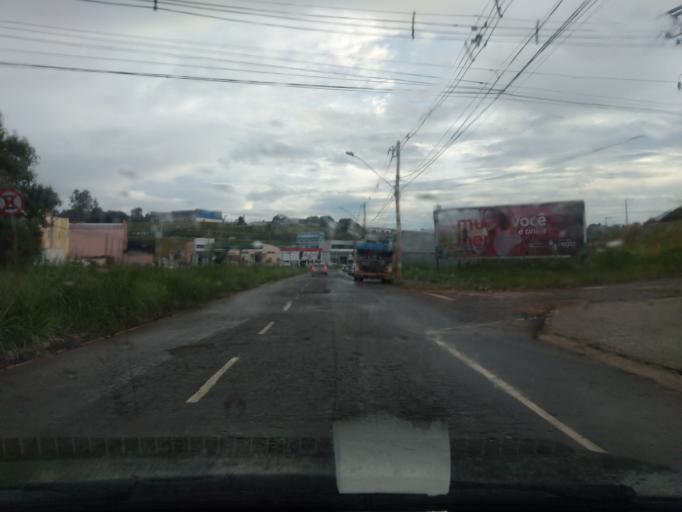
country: BR
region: Minas Gerais
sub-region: Varginha
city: Varginha
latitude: -21.5722
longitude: -45.4469
